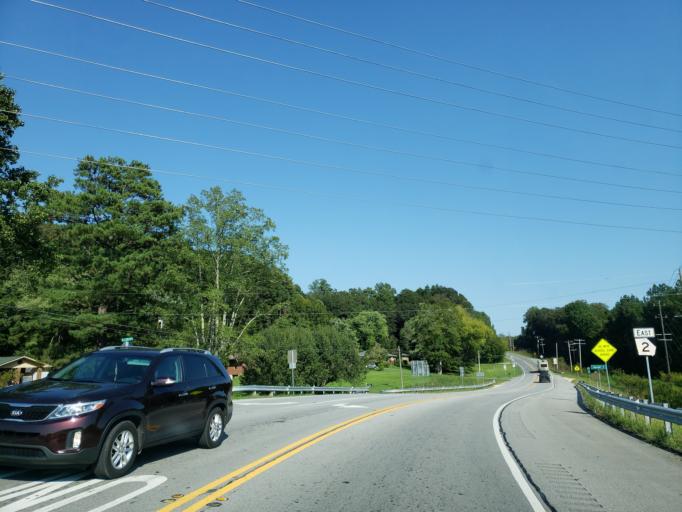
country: US
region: Georgia
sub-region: Catoosa County
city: Ringgold
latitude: 34.9059
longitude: -85.0772
